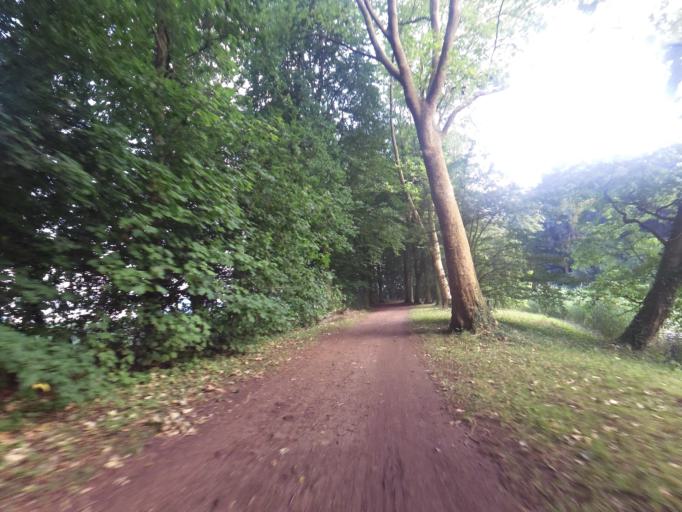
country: NL
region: Gelderland
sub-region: Oude IJsselstreek
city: Gendringen
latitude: 51.8532
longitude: 6.4086
